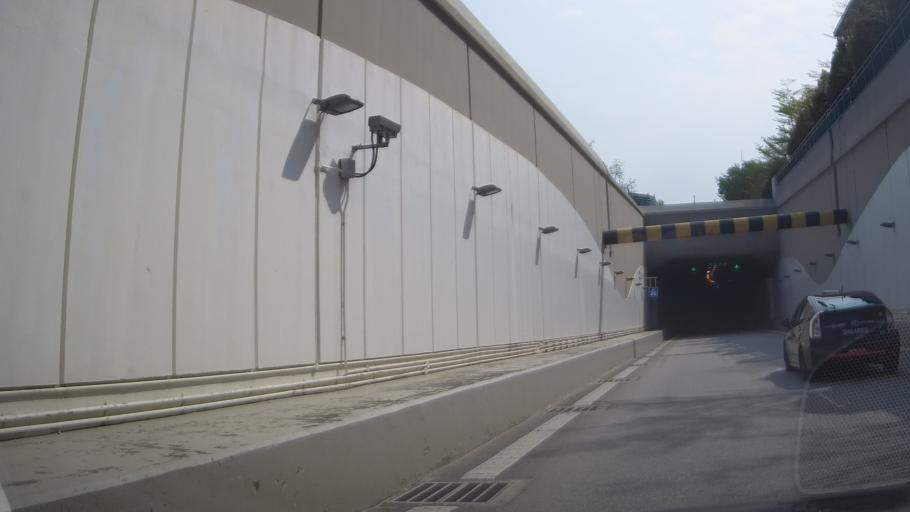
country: SG
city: Singapore
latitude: 1.2756
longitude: 103.8667
